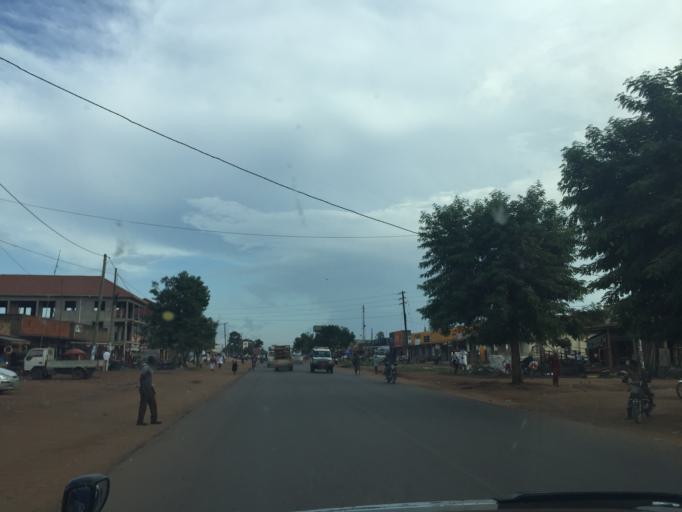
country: UG
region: Central Region
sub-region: Luwero District
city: Luwero
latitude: 0.8460
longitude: 32.4906
